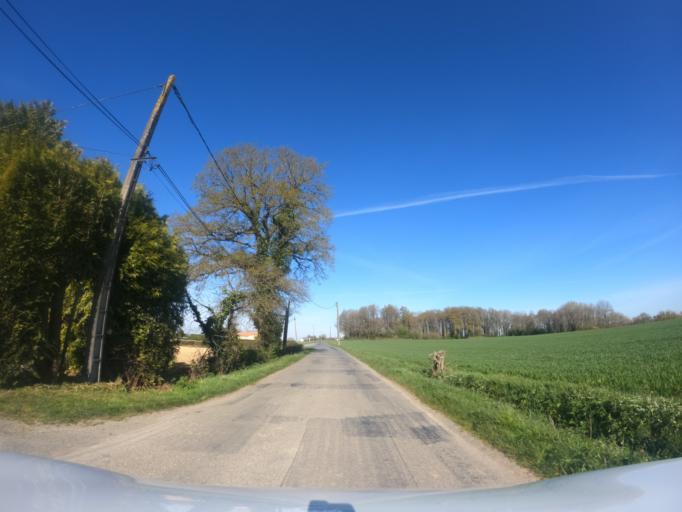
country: FR
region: Pays de la Loire
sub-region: Departement de la Vendee
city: Saint-Pierre-du-Chemin
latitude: 46.6901
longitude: -0.7109
